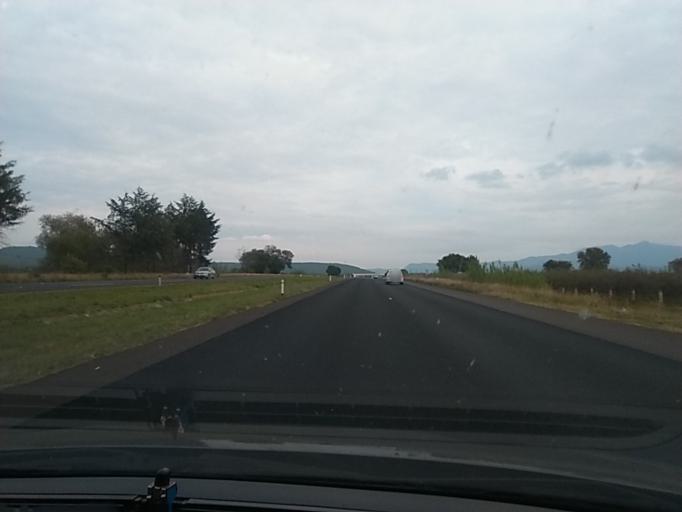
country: MX
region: Michoacan
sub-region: Jimenez
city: Copandaro (Copandaro del Cuatro)
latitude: 19.9151
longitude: -101.5905
